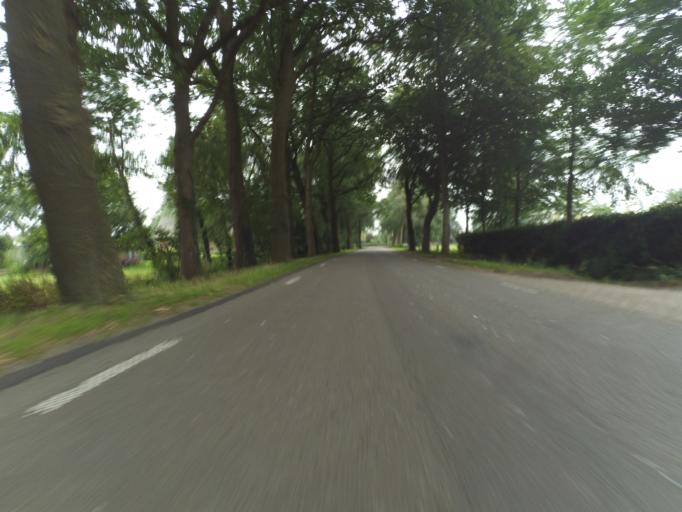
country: NL
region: Gelderland
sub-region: Gemeente Barneveld
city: Kootwijkerbroek
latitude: 52.1607
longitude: 5.6344
